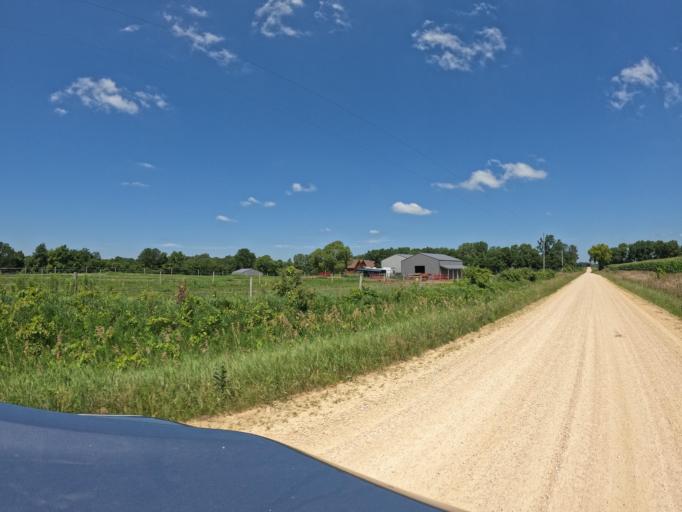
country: US
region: Iowa
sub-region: Clinton County
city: De Witt
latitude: 41.7649
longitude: -90.4325
